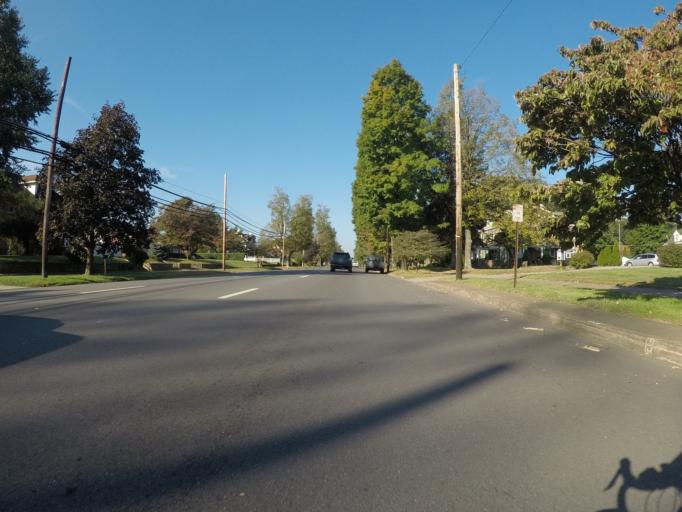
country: US
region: West Virginia
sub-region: Cabell County
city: Huntington
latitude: 38.4291
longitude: -82.4034
